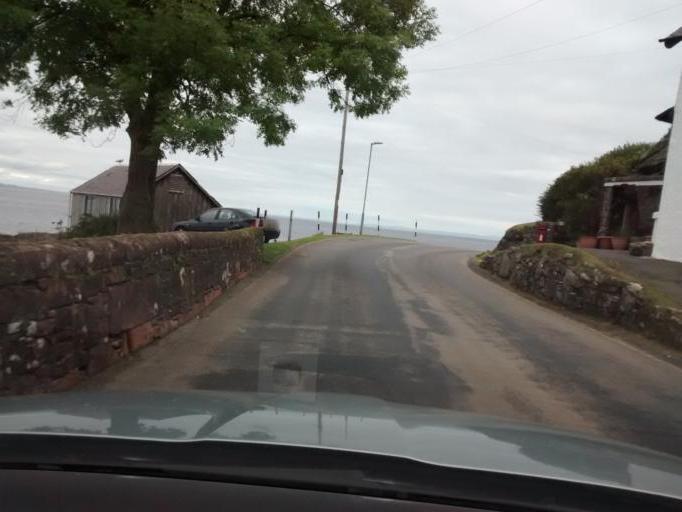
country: GB
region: Scotland
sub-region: North Ayrshire
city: Isle of Arran
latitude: 55.6443
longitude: -5.1399
